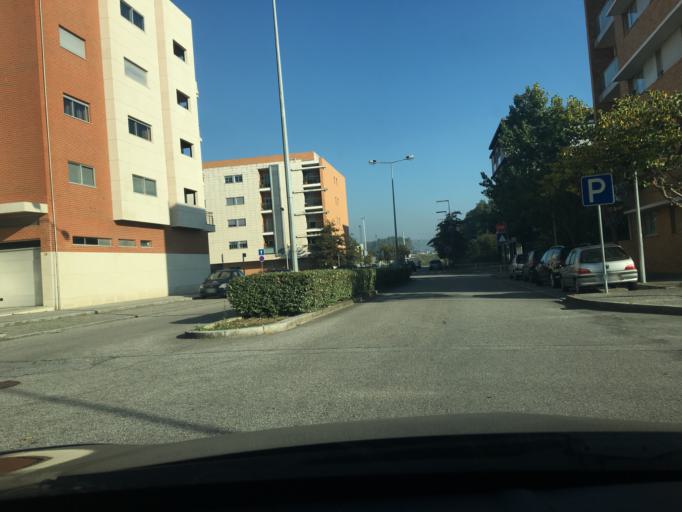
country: PT
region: Porto
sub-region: Maia
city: Anta
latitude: 41.2672
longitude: -8.6145
